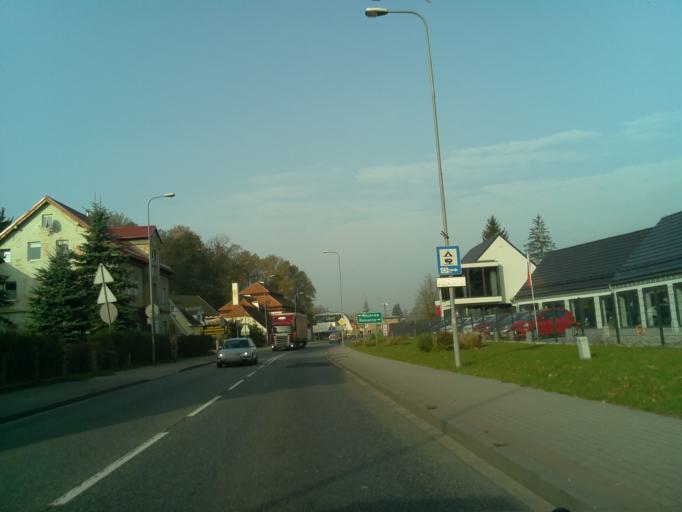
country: PL
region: Lower Silesian Voivodeship
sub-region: Powiat jeleniogorski
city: Myslakowice
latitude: 50.9074
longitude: 15.8372
